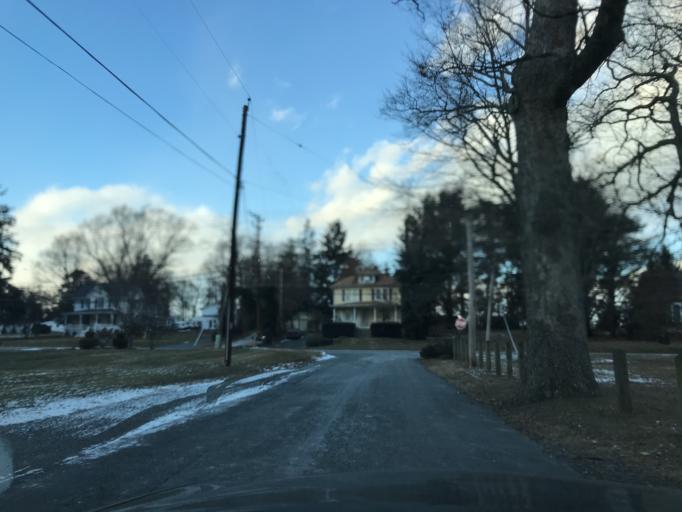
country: US
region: Maryland
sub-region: Harford County
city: Bel Air North
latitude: 39.5838
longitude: -76.3835
